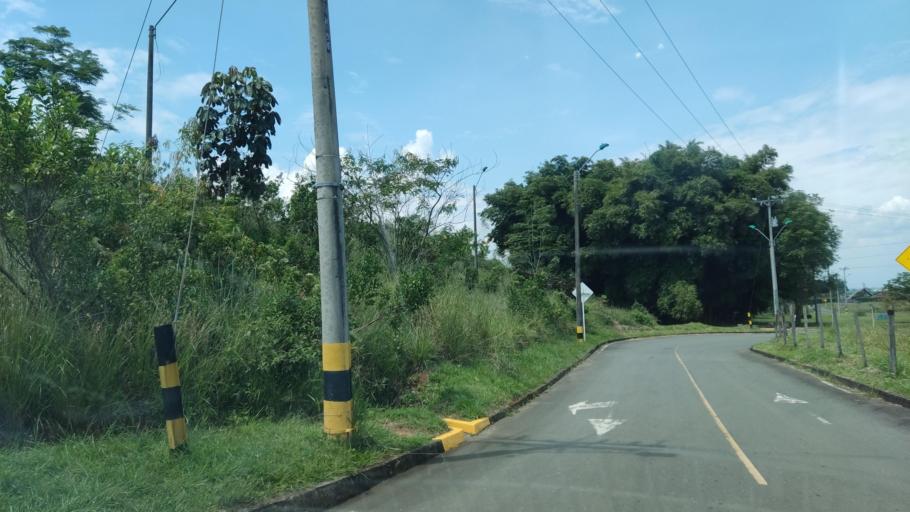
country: CO
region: Valle del Cauca
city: Jamundi
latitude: 3.3031
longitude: -76.5559
